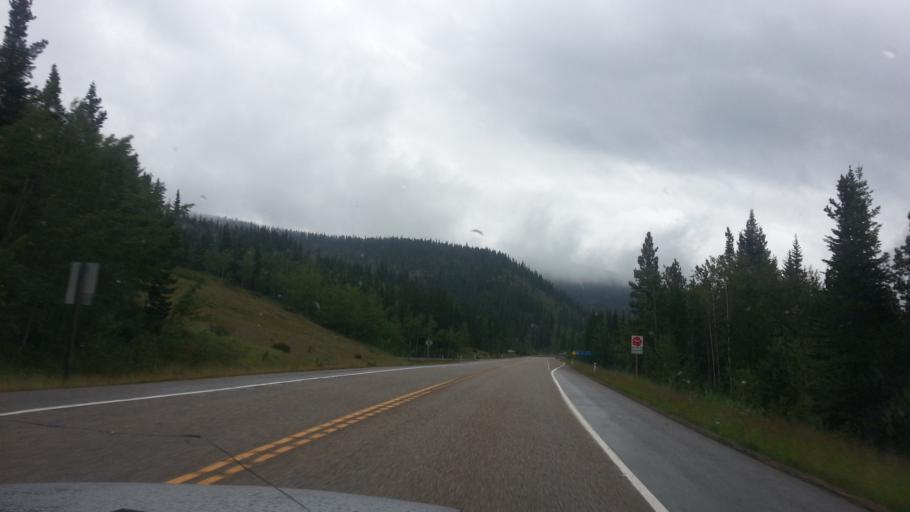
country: CA
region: Alberta
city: Cochrane
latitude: 50.8637
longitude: -114.7929
